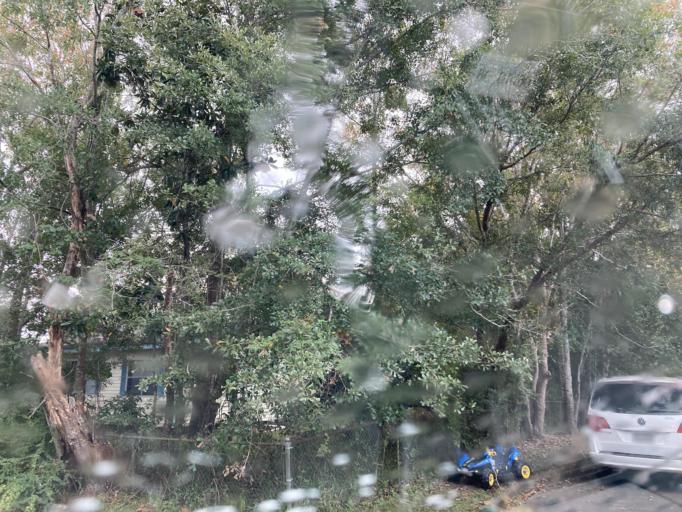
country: US
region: Mississippi
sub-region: Jackson County
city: Gulf Hills
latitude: 30.4414
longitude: -88.8347
